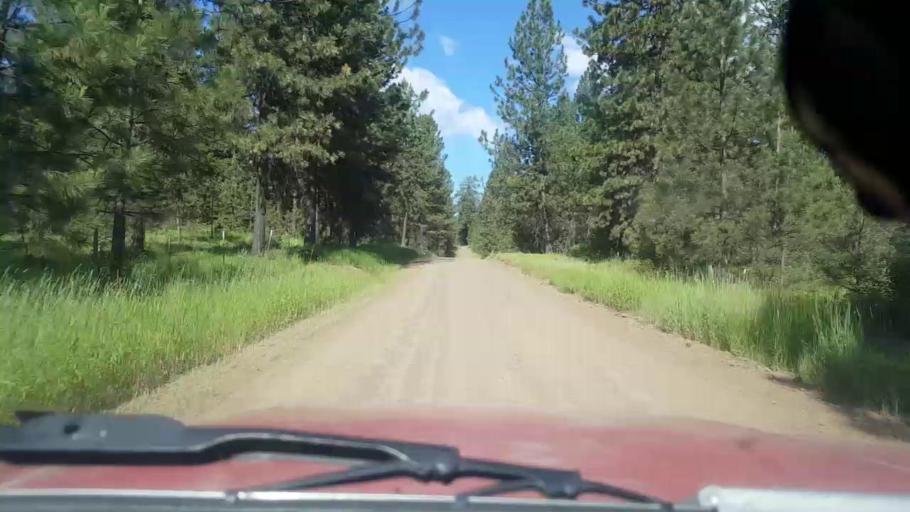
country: US
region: Washington
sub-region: Asotin County
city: Asotin
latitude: 46.0371
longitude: -117.4138
